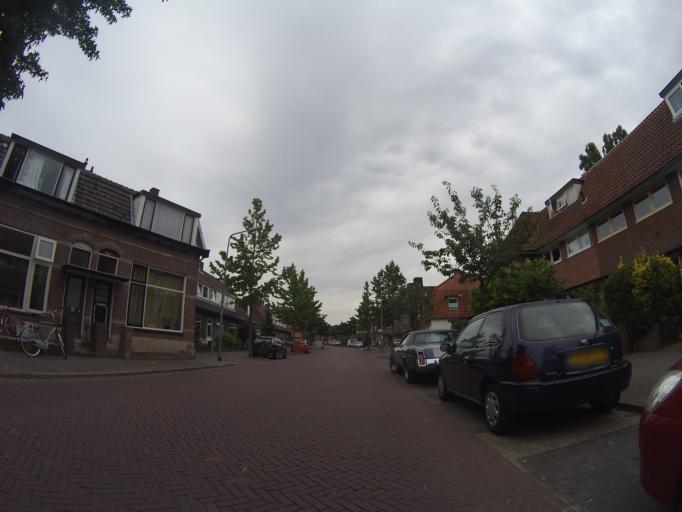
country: NL
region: North Holland
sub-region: Gemeente Hilversum
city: Hilversum
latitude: 52.2265
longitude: 5.1855
